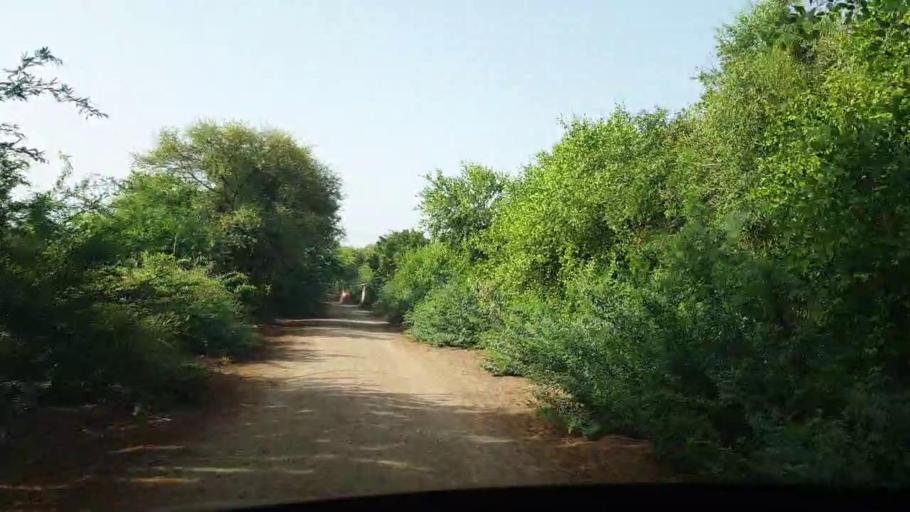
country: PK
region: Sindh
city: Nawabshah
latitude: 26.2441
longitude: 68.4497
